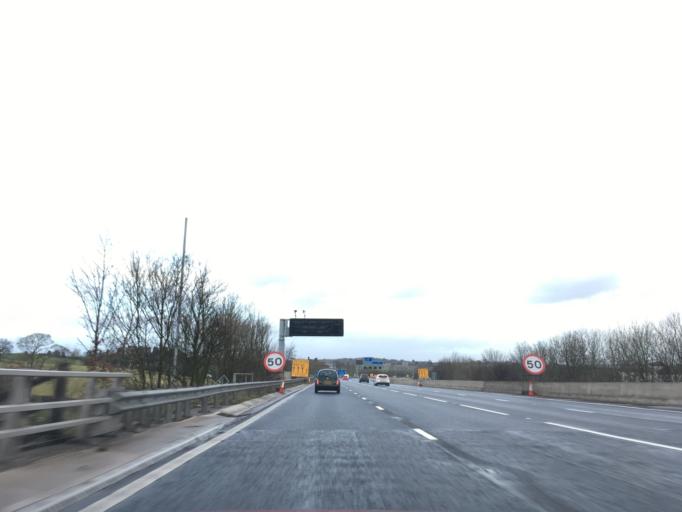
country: GB
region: England
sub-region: Worcestershire
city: Bromsgrove
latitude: 52.3333
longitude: -2.0846
